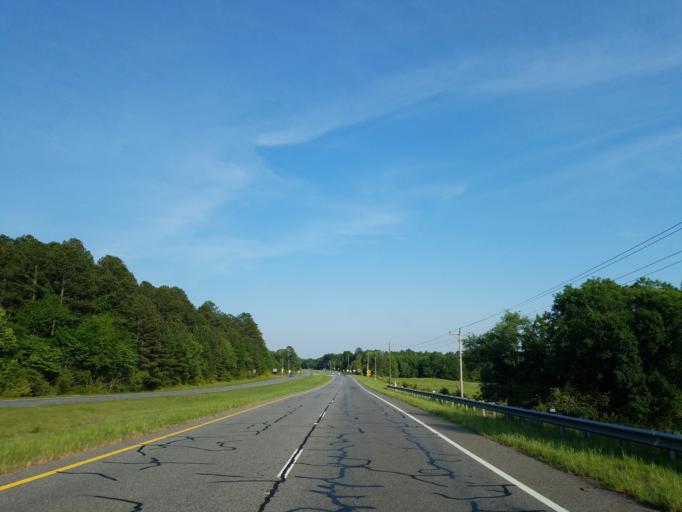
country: US
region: Georgia
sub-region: Chattooga County
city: Summerville
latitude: 34.4170
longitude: -85.2373
